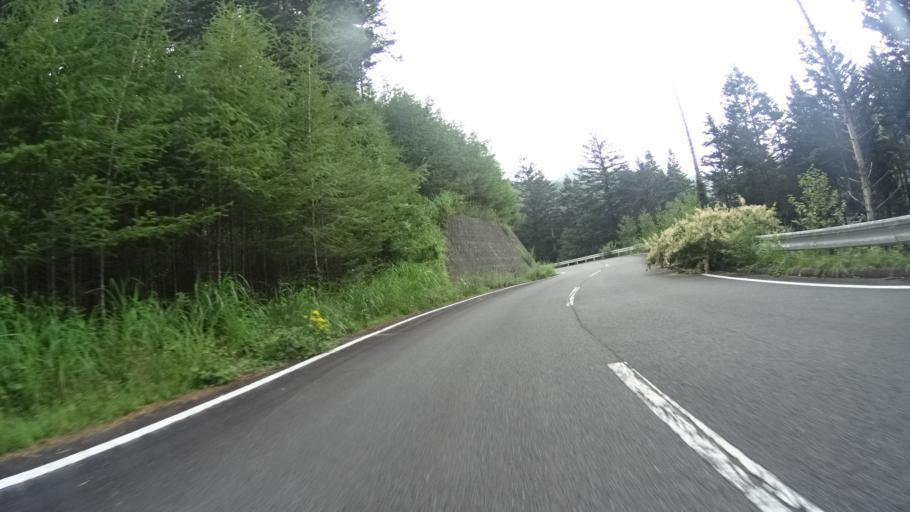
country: JP
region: Yamanashi
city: Enzan
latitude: 35.8041
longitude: 138.6520
